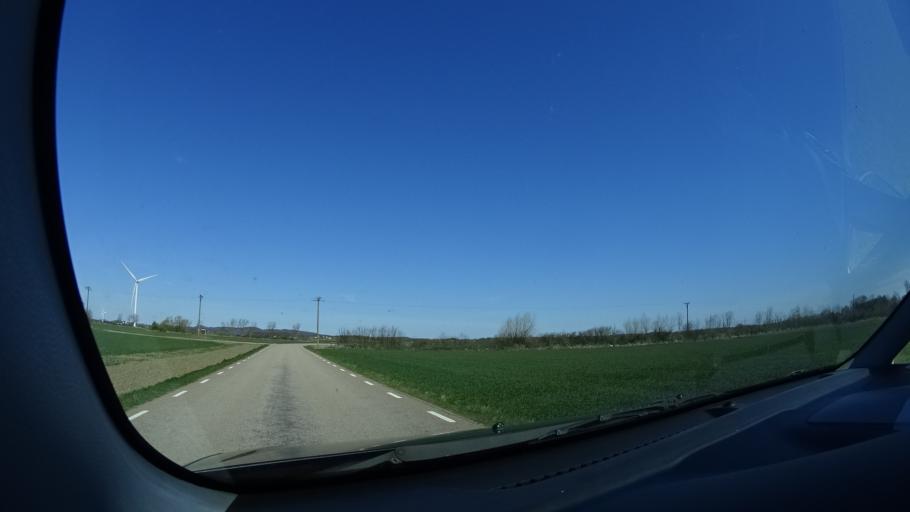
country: SE
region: Skane
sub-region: Hoganas Kommun
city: Hoganas
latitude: 56.2296
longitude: 12.5876
